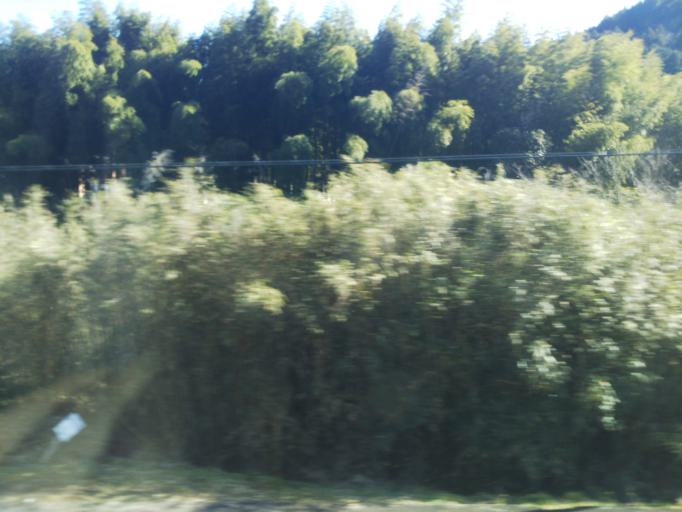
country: JP
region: Kochi
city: Nakamura
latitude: 33.1212
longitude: 133.1181
